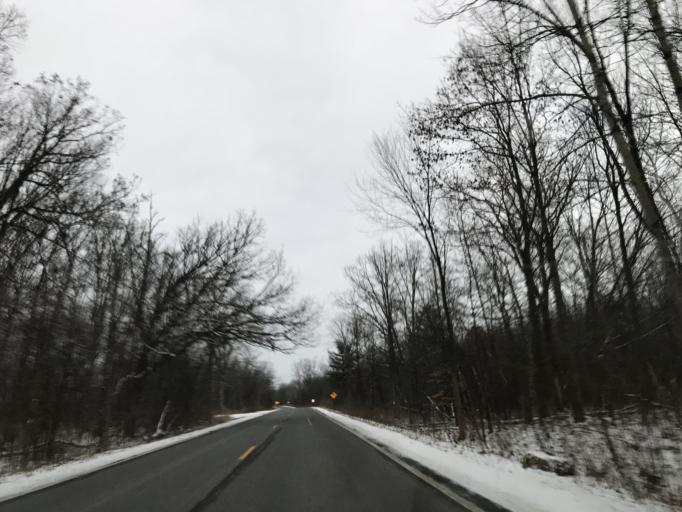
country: US
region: Michigan
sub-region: Oakland County
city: South Lyon
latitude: 42.3582
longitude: -83.6727
